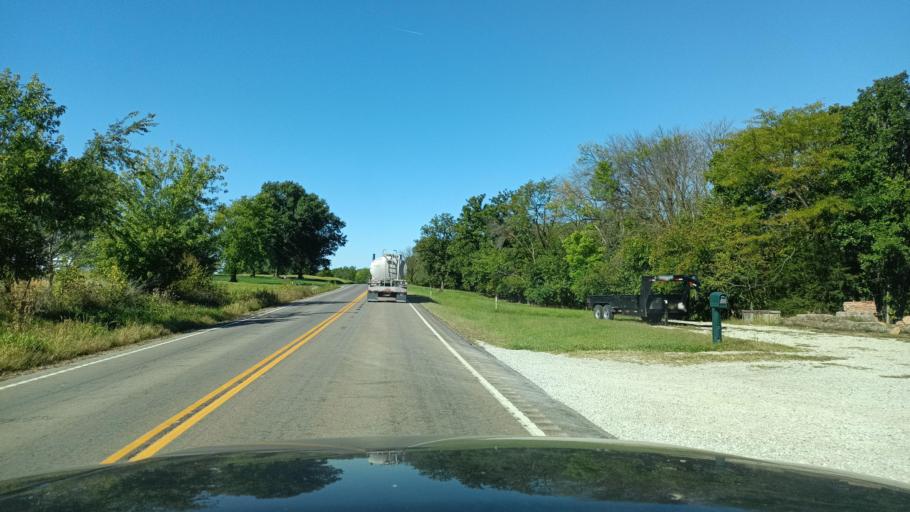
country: US
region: Missouri
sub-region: Scotland County
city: Memphis
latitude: 40.4563
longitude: -92.1443
